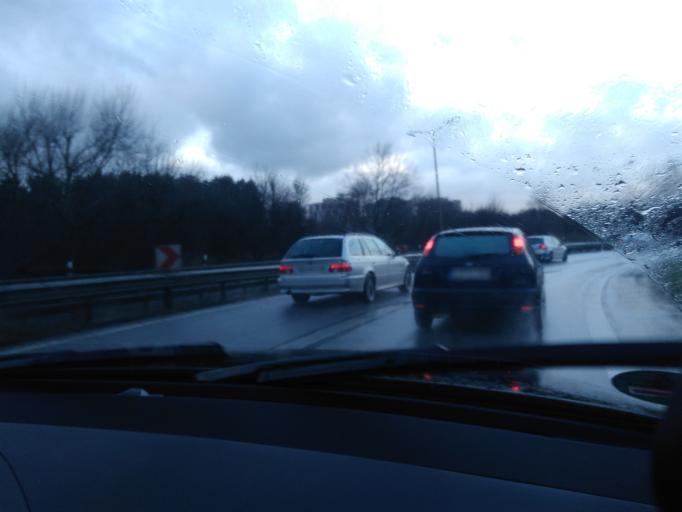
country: DE
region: Hamburg
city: Langenhorn
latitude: 53.6502
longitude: 9.9845
